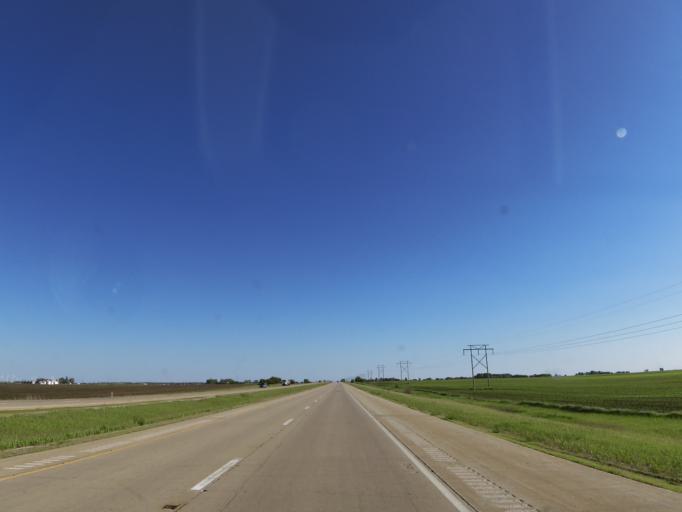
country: US
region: Illinois
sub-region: Woodford County
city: Minonk
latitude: 40.9535
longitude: -89.0567
